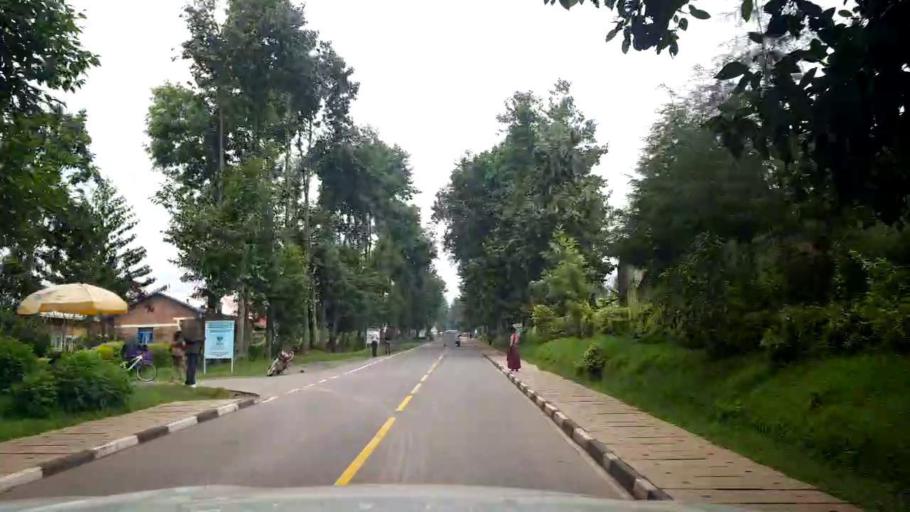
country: RW
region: Northern Province
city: Musanze
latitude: -1.4616
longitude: 29.6137
